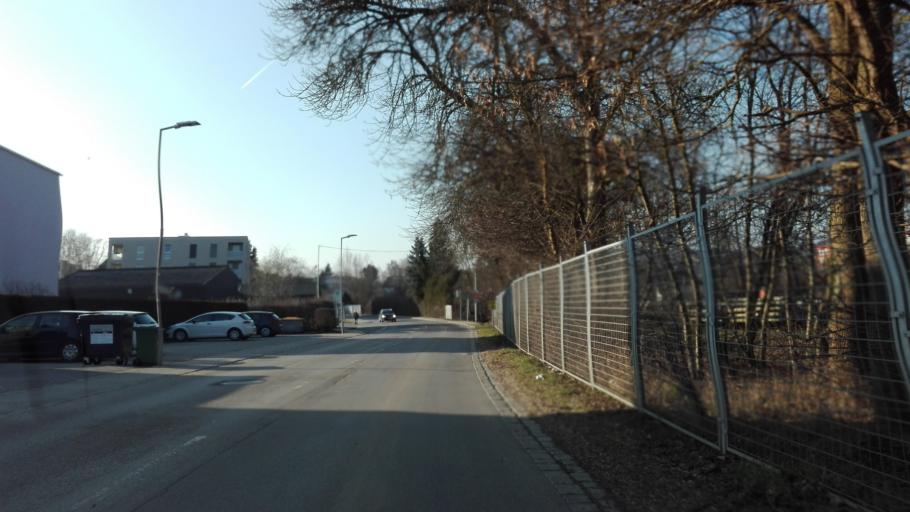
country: AT
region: Upper Austria
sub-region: Politischer Bezirk Linz-Land
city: Leonding
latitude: 48.2935
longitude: 14.2642
